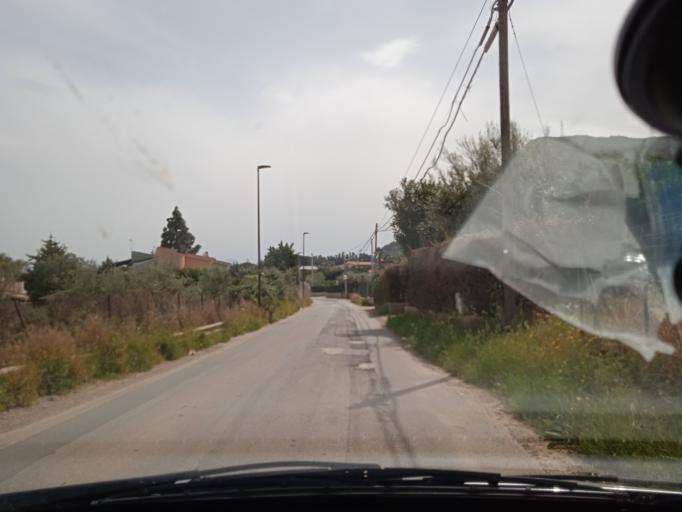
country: IT
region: Sicily
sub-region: Palermo
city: Torre Colonna-Sperone
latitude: 38.0271
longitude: 13.5739
